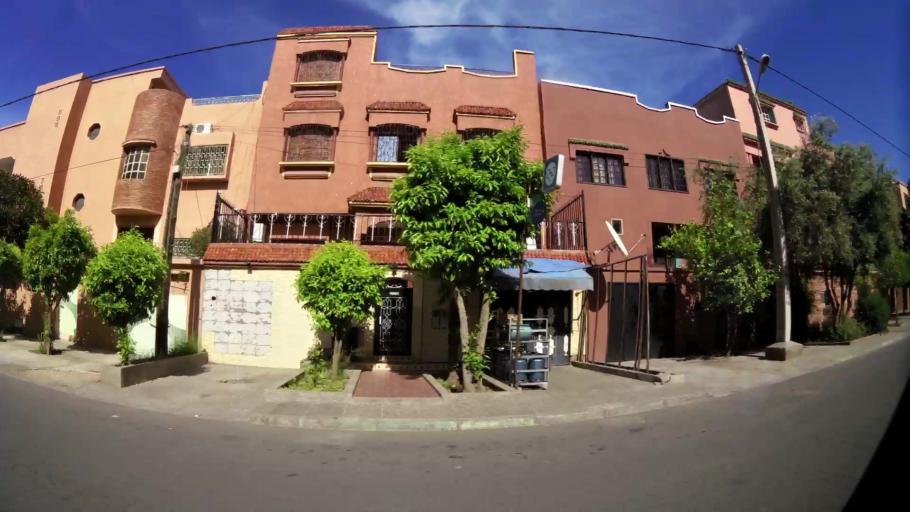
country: MA
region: Marrakech-Tensift-Al Haouz
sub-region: Marrakech
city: Marrakesh
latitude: 31.6535
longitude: -8.0107
